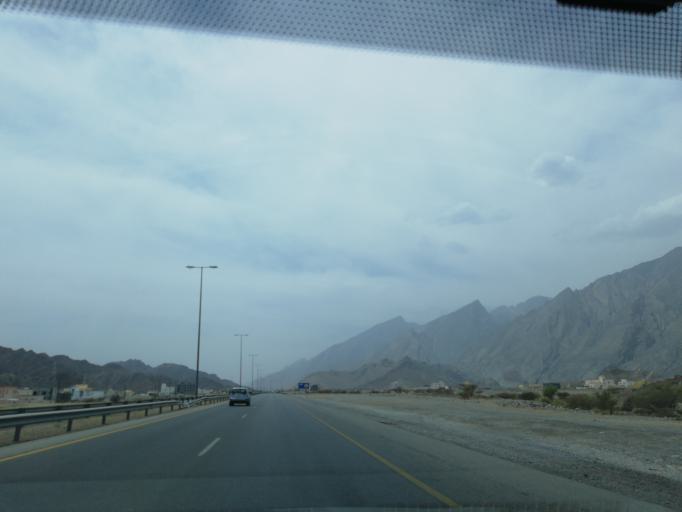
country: OM
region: Muhafazat ad Dakhiliyah
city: Sufalat Sama'il
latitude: 23.1981
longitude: 57.8837
